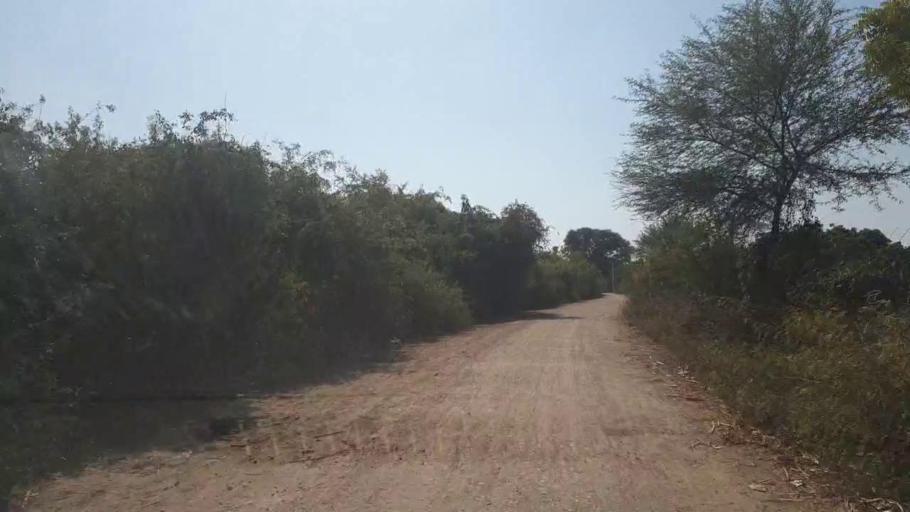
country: PK
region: Sindh
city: Chambar
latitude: 25.3127
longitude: 68.7191
